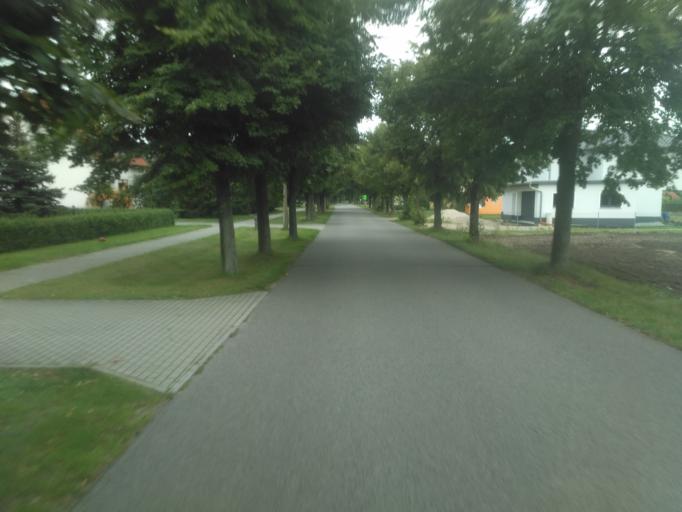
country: DE
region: Brandenburg
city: Welzow
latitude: 51.5187
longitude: 14.1814
